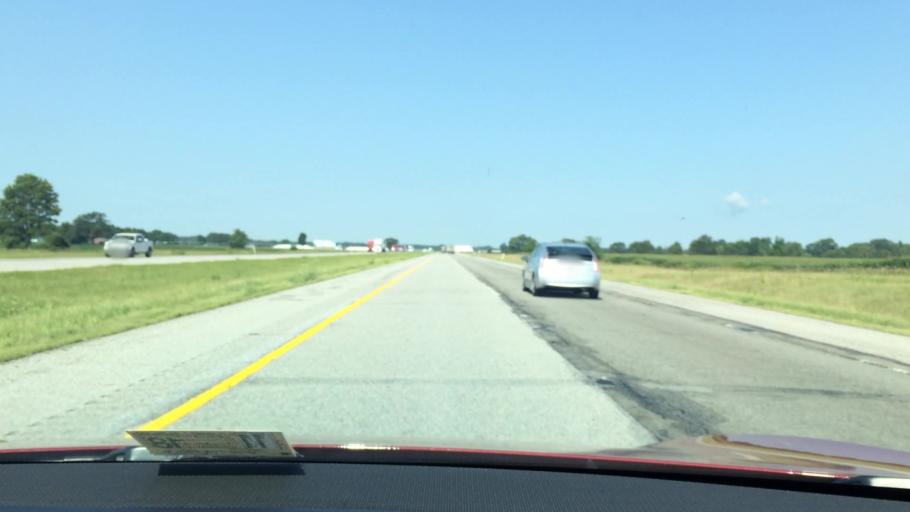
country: US
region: Michigan
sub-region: Saint Joseph County
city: Sturgis
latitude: 41.7456
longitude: -85.5193
